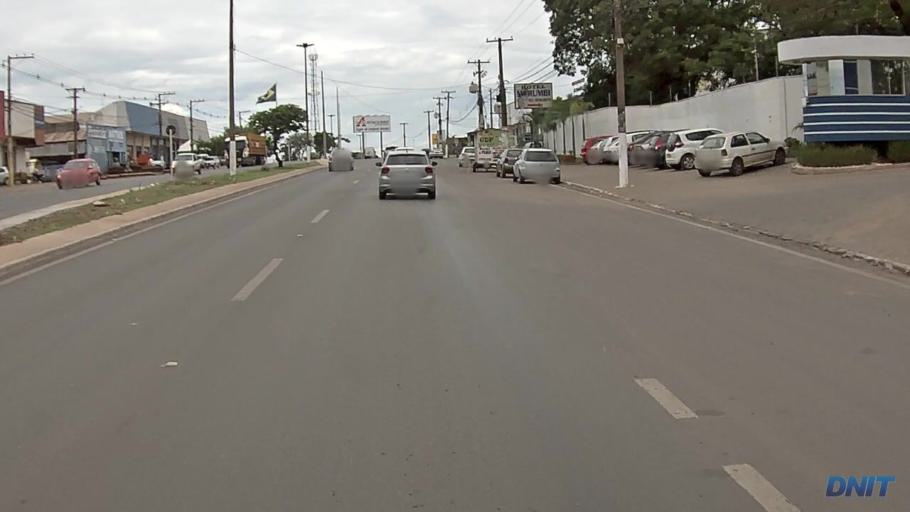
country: BR
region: Mato Grosso
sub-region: Varzea Grande
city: Varzea Grande
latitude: -15.6411
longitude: -56.1664
